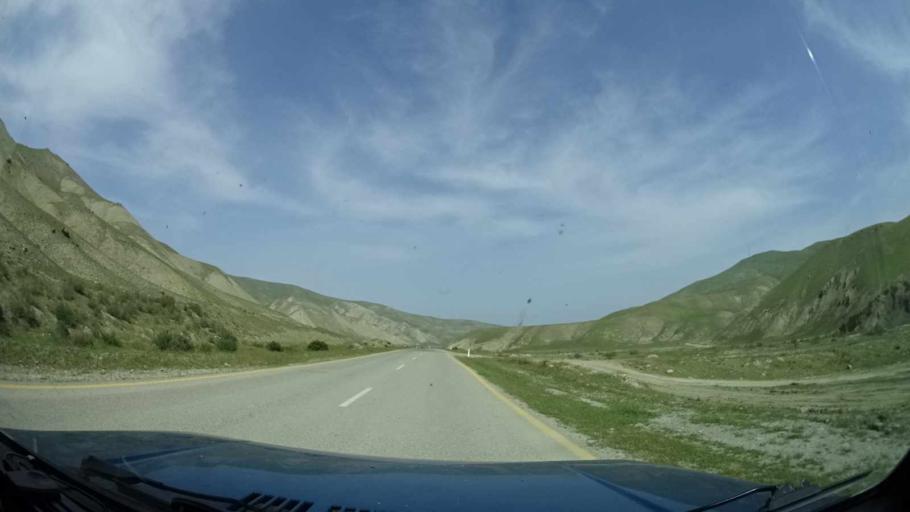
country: AZ
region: Xizi
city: Kilyazi
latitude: 40.8506
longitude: 49.2673
